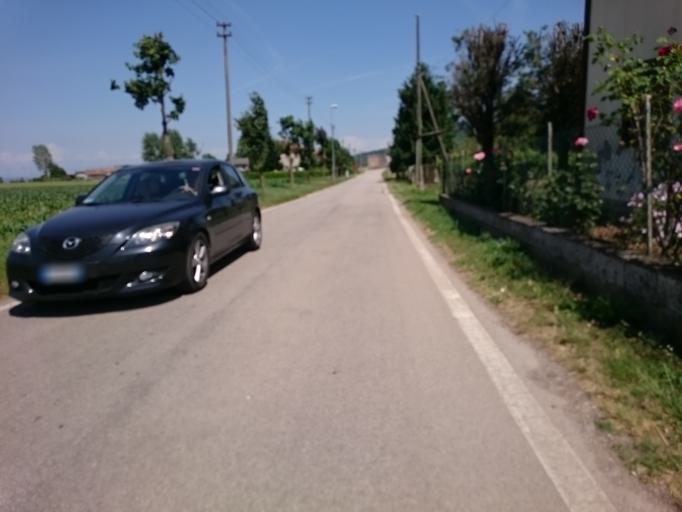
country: IT
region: Veneto
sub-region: Provincia di Padova
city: Lozzo Atestino
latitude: 45.2614
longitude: 11.6188
